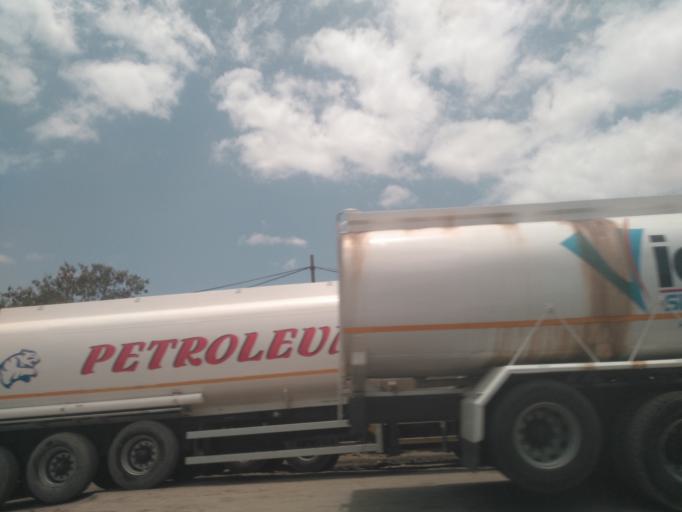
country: TZ
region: Dar es Salaam
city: Dar es Salaam
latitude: -6.8430
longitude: 39.2937
